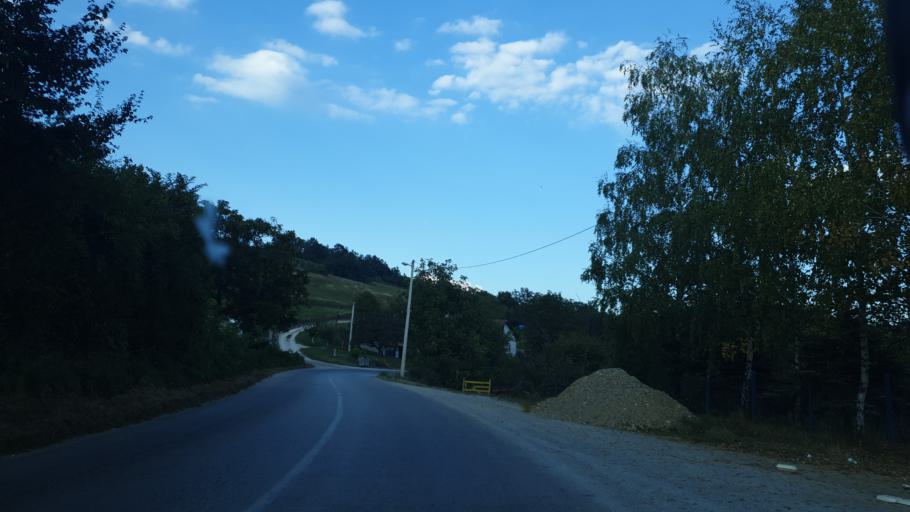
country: RS
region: Central Serbia
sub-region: Zlatiborski Okrug
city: Uzice
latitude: 43.8629
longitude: 19.8866
